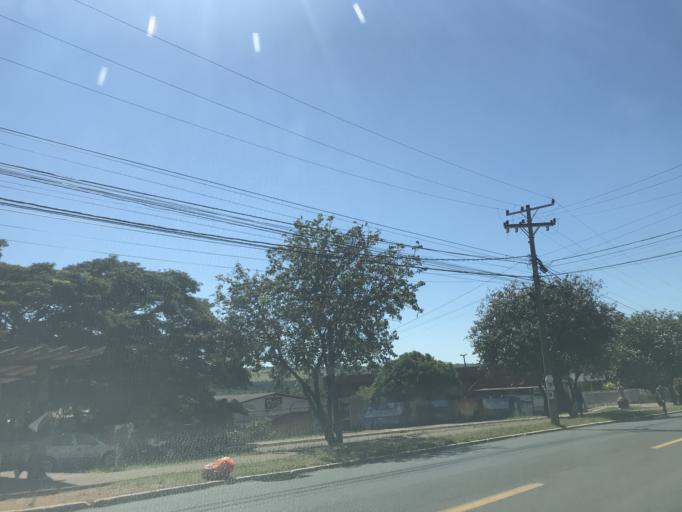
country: BR
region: Federal District
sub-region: Brasilia
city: Brasilia
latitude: -15.6500
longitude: -47.7875
